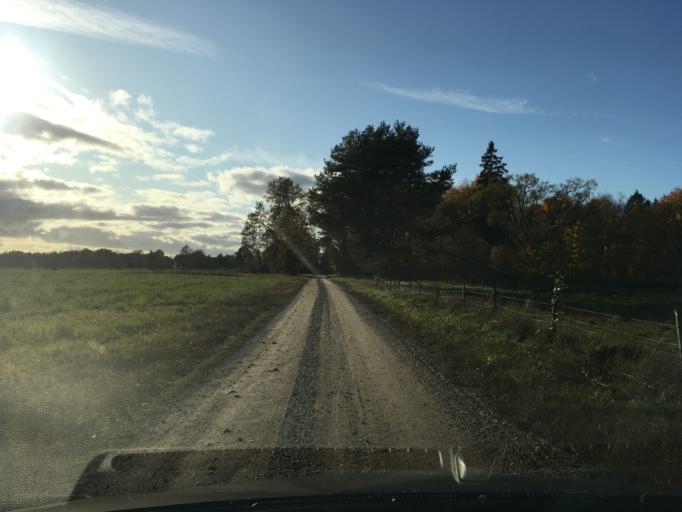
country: EE
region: Laeaene
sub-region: Lihula vald
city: Lihula
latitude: 58.5654
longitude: 23.7843
